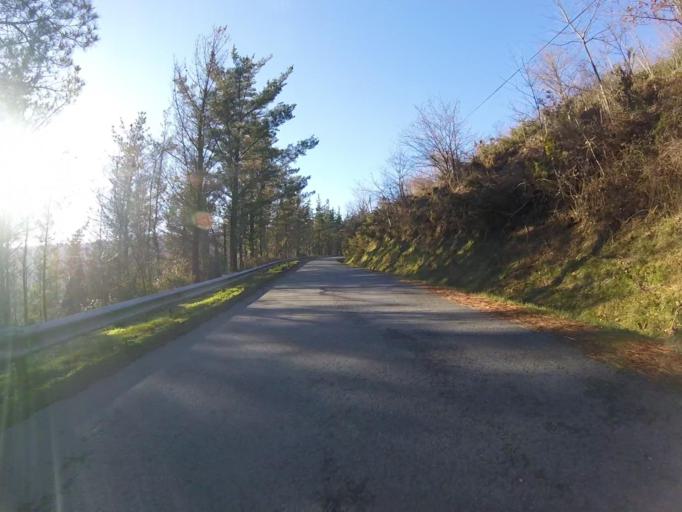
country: ES
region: Navarre
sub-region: Provincia de Navarra
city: Lesaka
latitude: 43.2675
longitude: -1.7443
